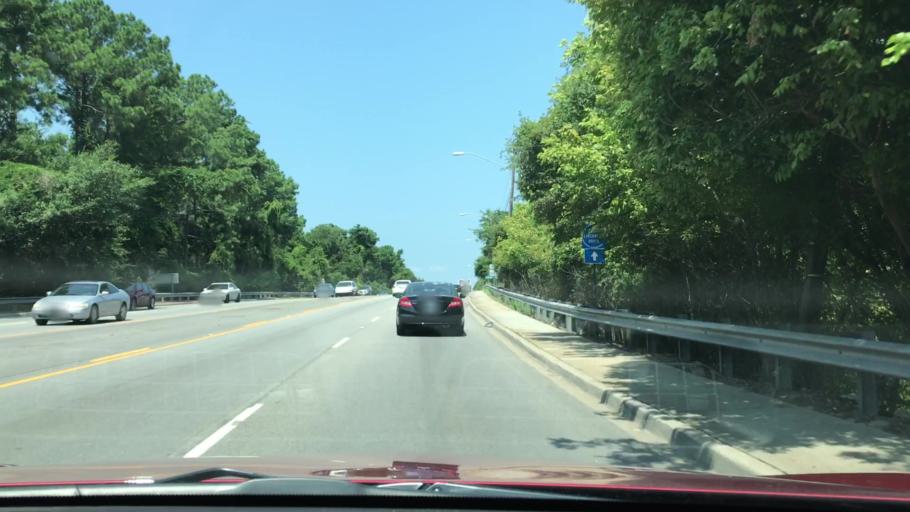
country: US
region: South Carolina
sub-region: Charleston County
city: North Charleston
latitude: 32.8552
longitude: -80.0234
